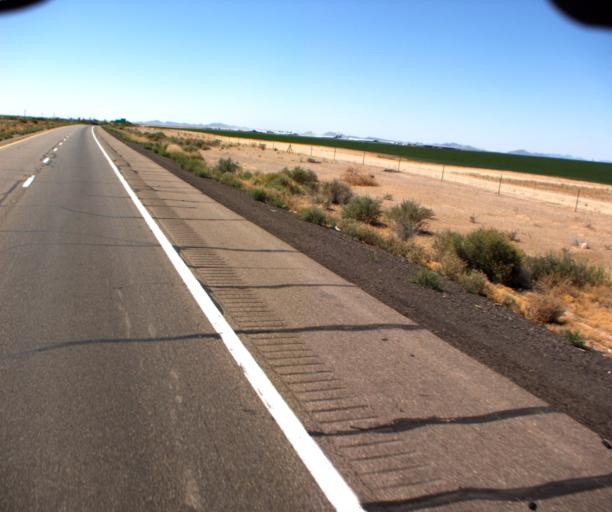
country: US
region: Arizona
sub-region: Maricopa County
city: Gila Bend
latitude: 32.9347
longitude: -112.7859
